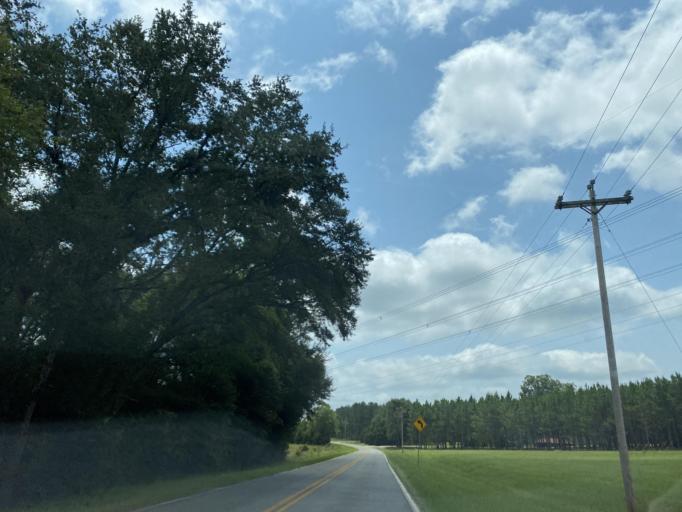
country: US
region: Georgia
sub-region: Wheeler County
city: Alamo
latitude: 32.1186
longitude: -82.7869
